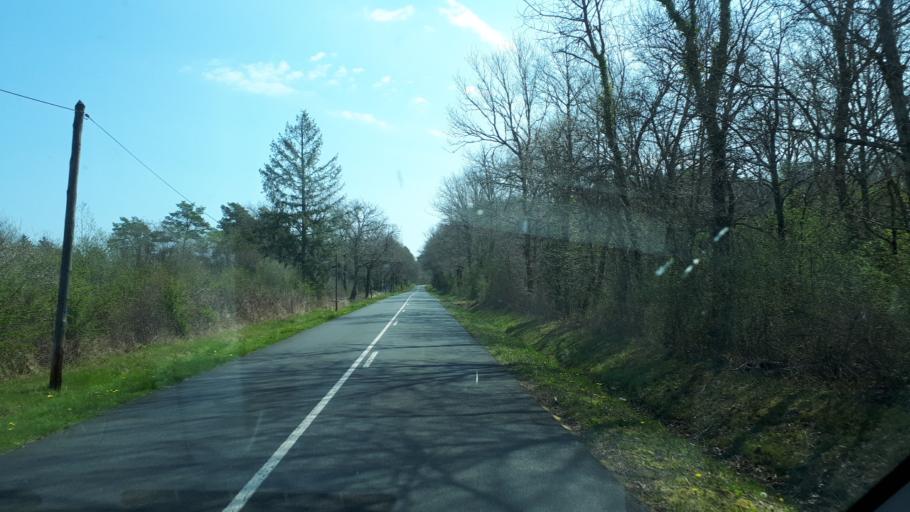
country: FR
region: Centre
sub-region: Departement du Loir-et-Cher
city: Selles-Saint-Denis
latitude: 47.3390
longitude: 1.9077
